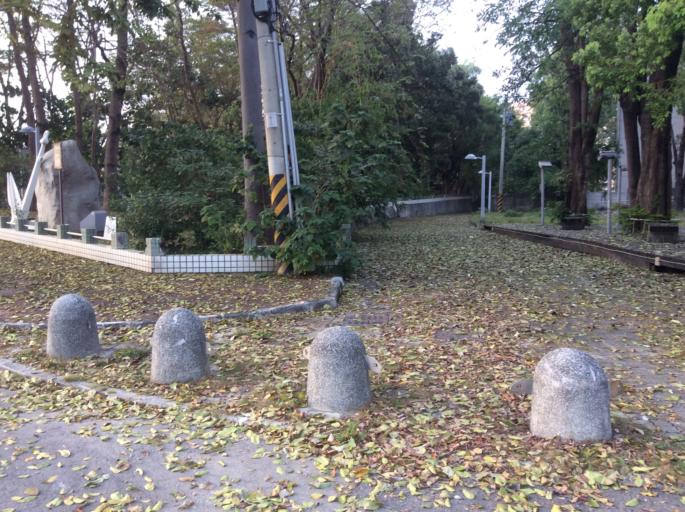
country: TW
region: Kaohsiung
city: Kaohsiung
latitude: 22.6938
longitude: 120.2894
